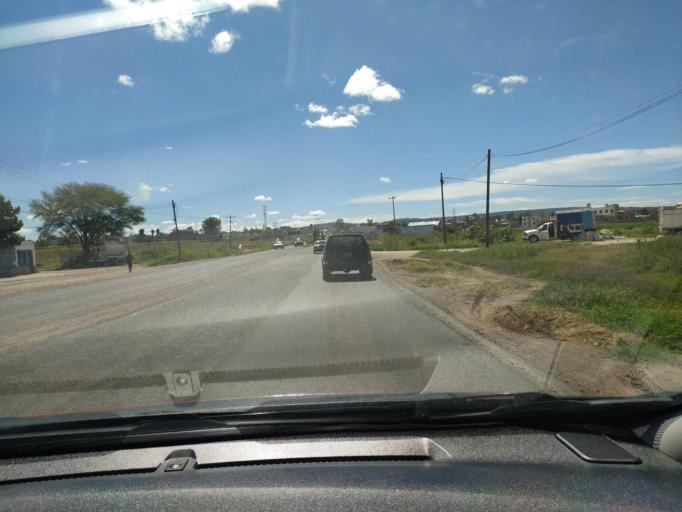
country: MX
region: Jalisco
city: San Miguel el Alto
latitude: 21.0370
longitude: -102.3977
